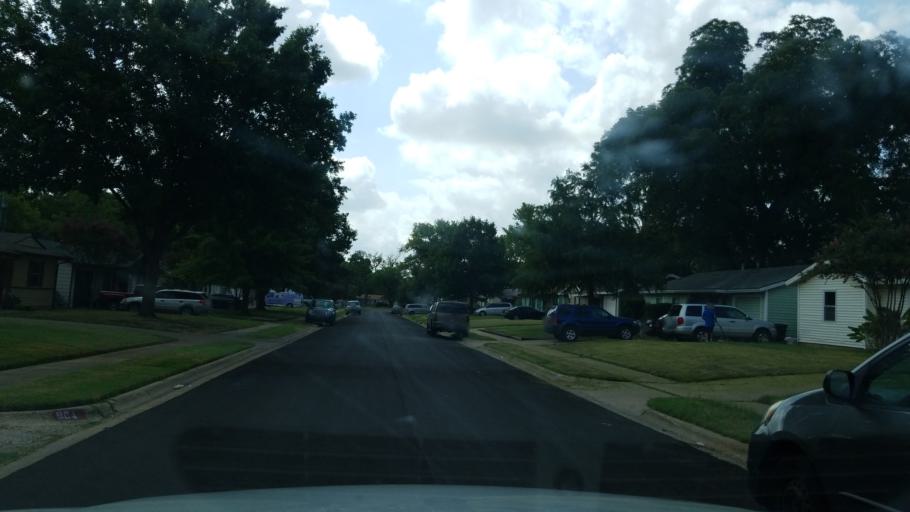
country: US
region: Texas
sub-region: Tarrant County
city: Euless
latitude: 32.8491
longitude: -97.0893
